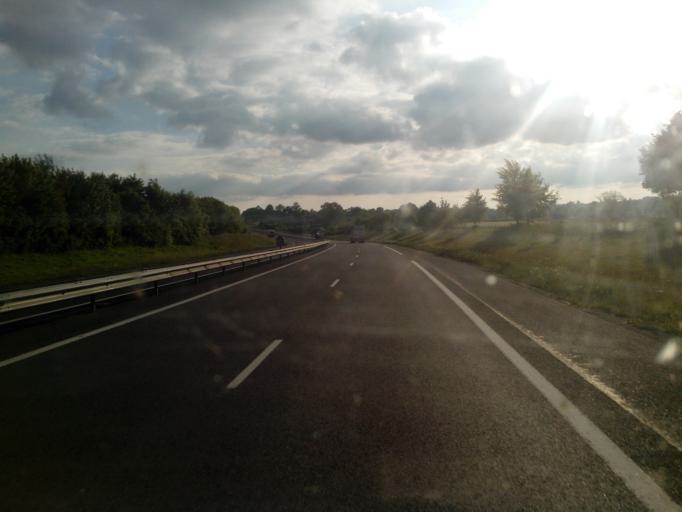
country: FR
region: Lower Normandy
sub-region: Departement du Calvados
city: Saint-Martin-des-Besaces
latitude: 49.0151
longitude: -0.8701
